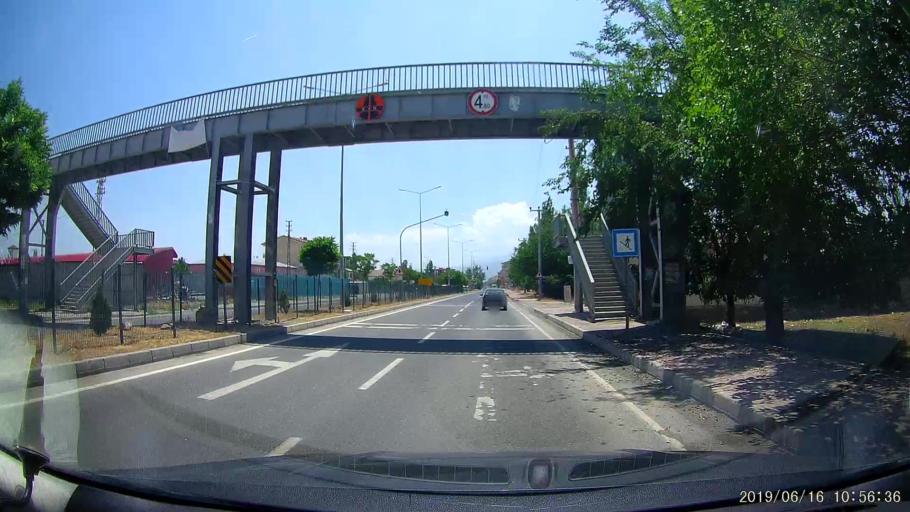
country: TR
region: Igdir
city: Igdir
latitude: 39.9283
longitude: 44.0248
